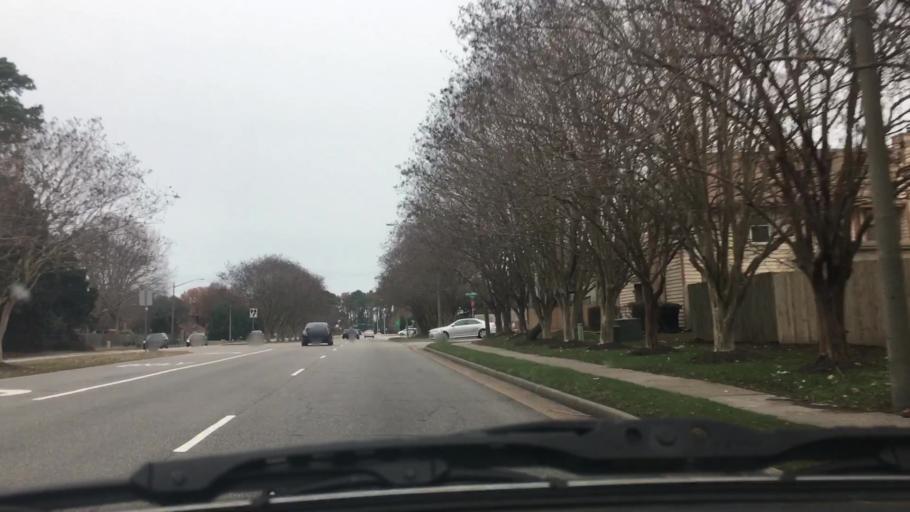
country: US
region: Virginia
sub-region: City of Chesapeake
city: Chesapeake
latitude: 36.8188
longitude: -76.1268
